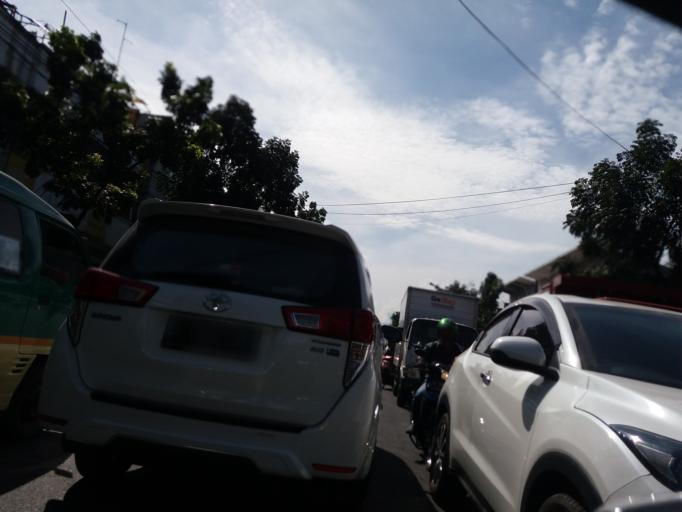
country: ID
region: West Java
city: Bandung
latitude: -6.9449
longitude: 107.6082
